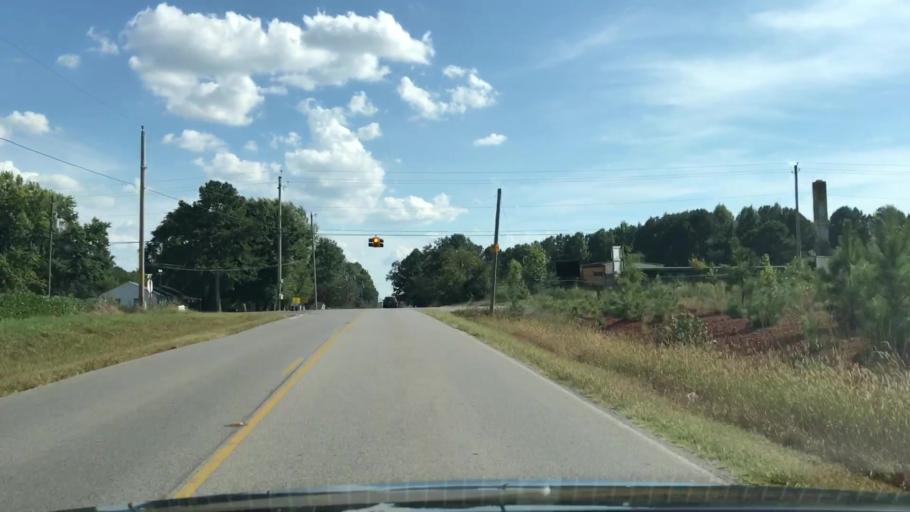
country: US
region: Alabama
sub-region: Madison County
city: Harvest
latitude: 34.8825
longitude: -86.7488
